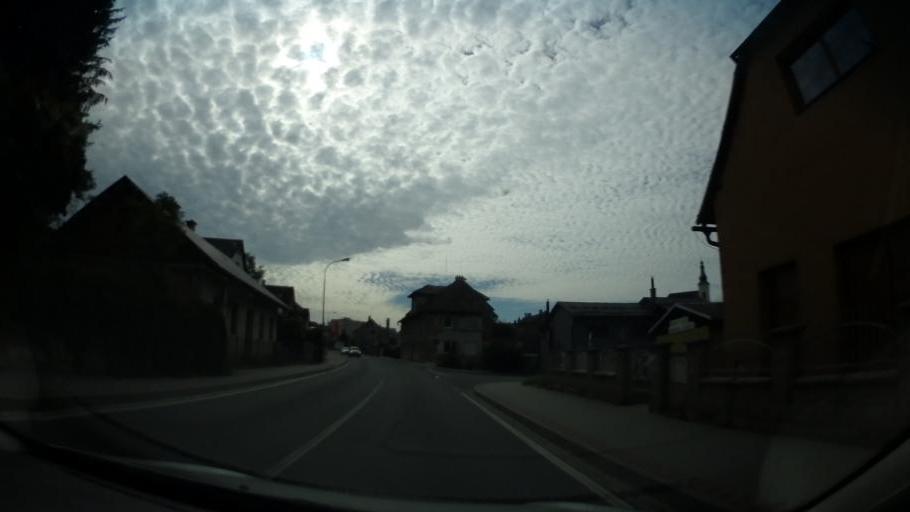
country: CZ
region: Olomoucky
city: Zabreh
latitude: 49.8853
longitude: 16.8719
